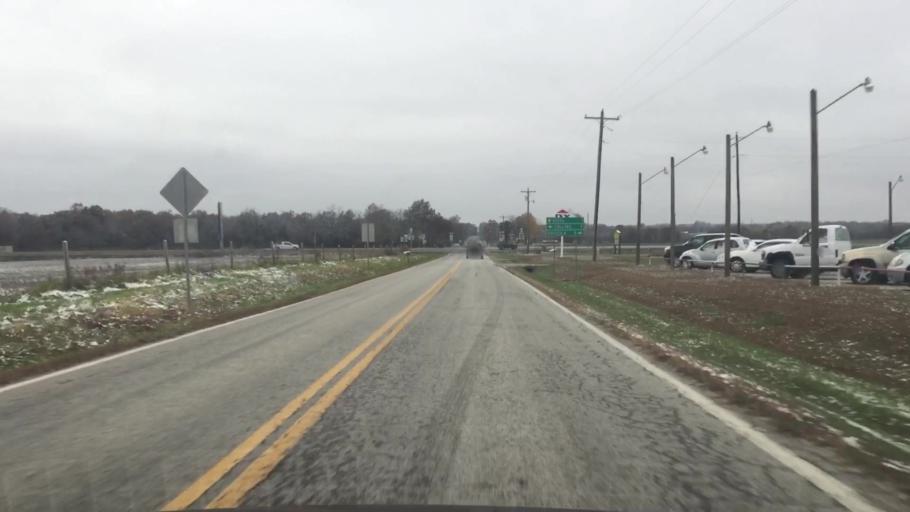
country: US
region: Missouri
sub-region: Saint Clair County
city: Osceola
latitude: 37.9899
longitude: -93.6496
